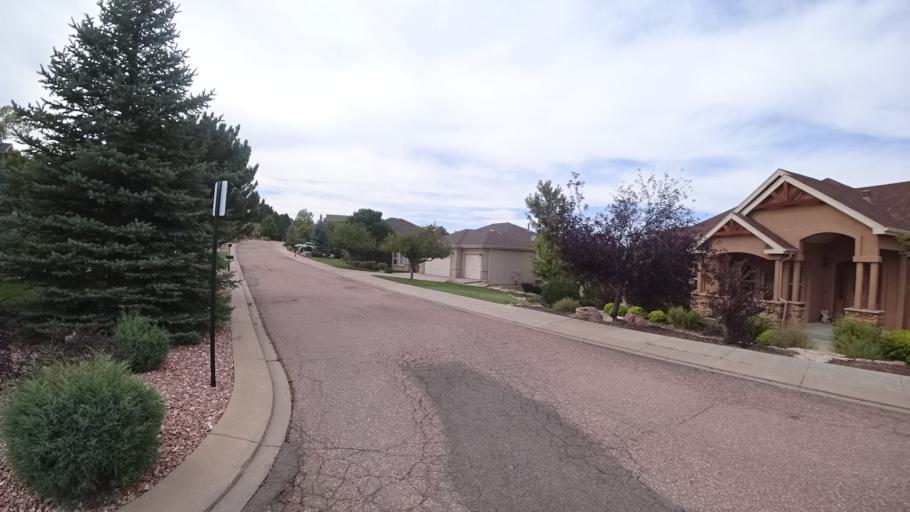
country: US
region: Colorado
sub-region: El Paso County
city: Colorado Springs
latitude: 38.9001
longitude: -104.7867
